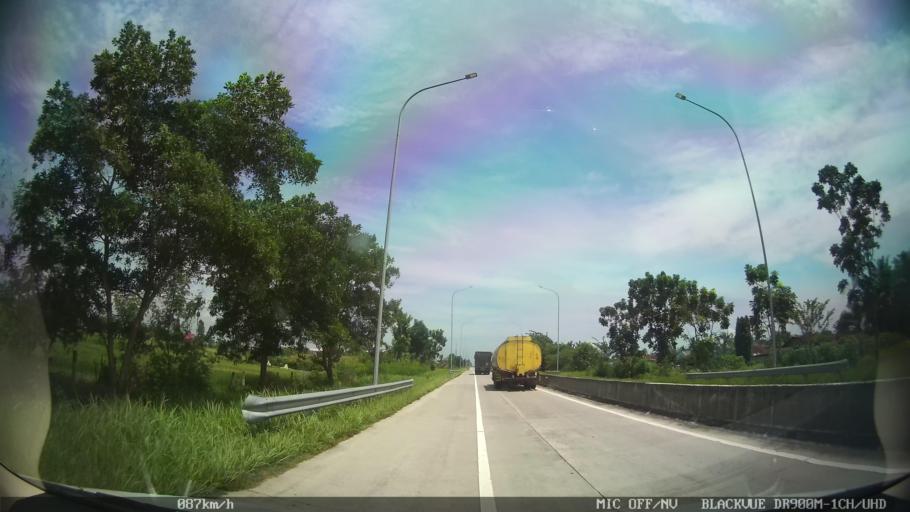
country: ID
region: North Sumatra
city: Perbaungan
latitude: 3.5491
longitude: 98.8889
